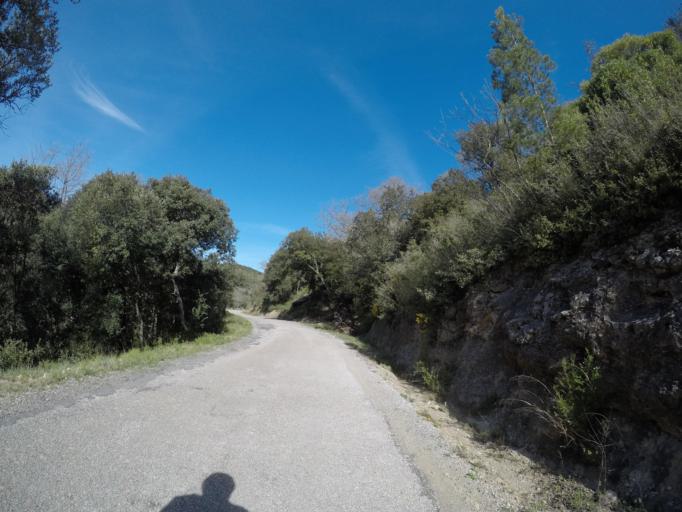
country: FR
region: Languedoc-Roussillon
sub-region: Departement des Pyrenees-Orientales
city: Thuir
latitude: 42.6293
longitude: 2.7030
